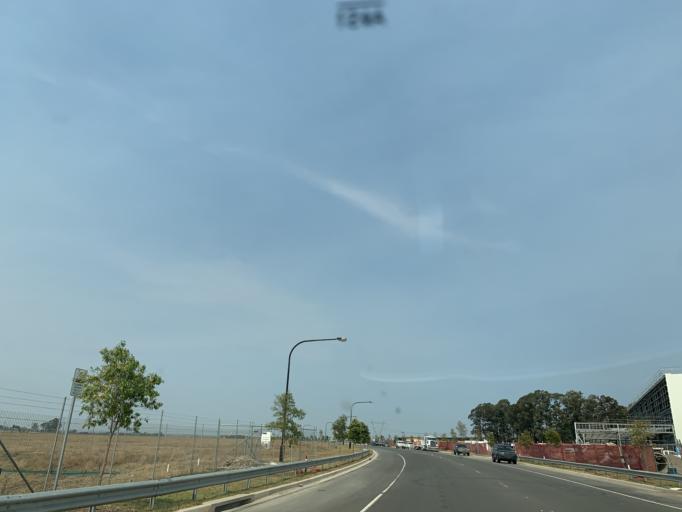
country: AU
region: New South Wales
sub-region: Blacktown
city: Hassall Grove
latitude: -33.7187
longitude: 150.8274
